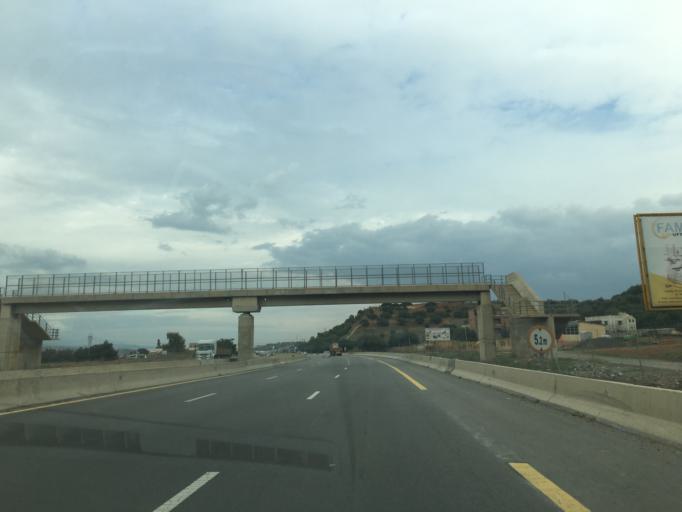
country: DZ
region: Bouira
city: Bouira
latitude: 36.3109
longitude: 4.0409
